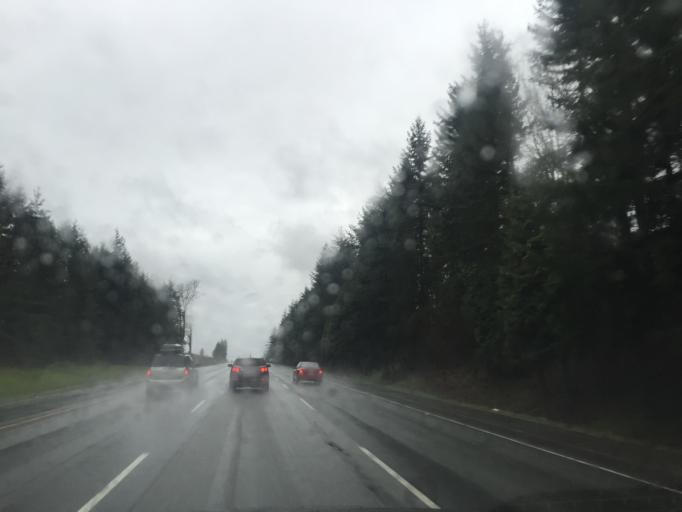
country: CA
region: British Columbia
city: Langley
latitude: 49.1299
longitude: -122.5654
